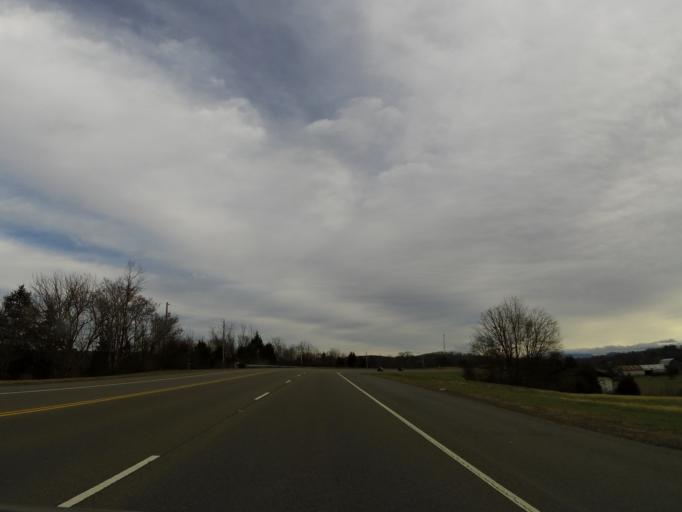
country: US
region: Tennessee
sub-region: Cocke County
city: Newport
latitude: 35.9865
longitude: -83.1535
